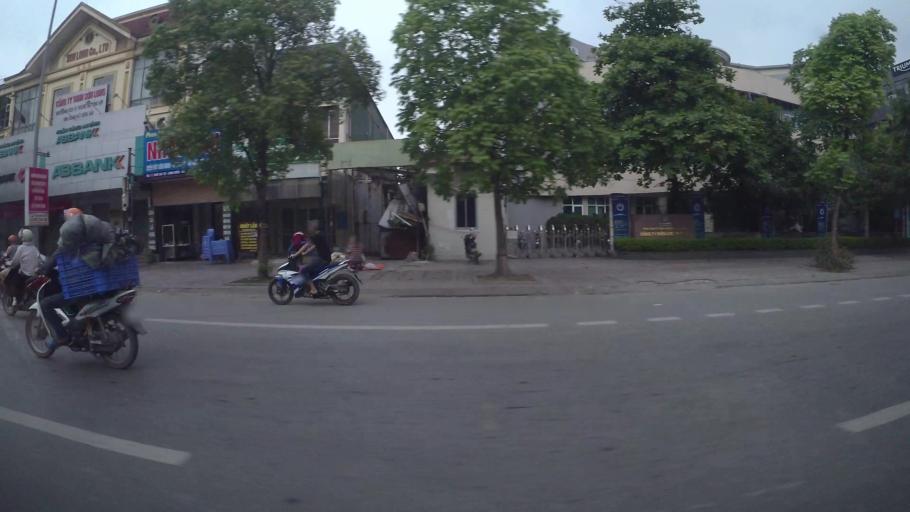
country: VN
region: Ha Noi
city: Hoan Kiem
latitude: 21.0582
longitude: 105.8910
